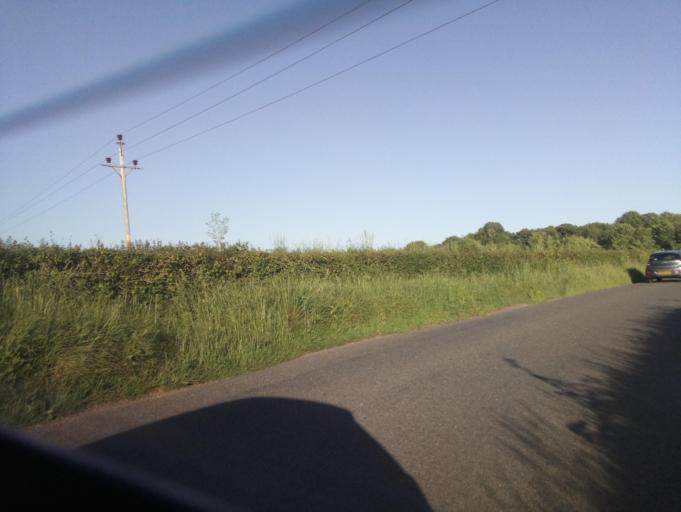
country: GB
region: England
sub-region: Devon
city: Topsham
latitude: 50.7266
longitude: -3.4001
